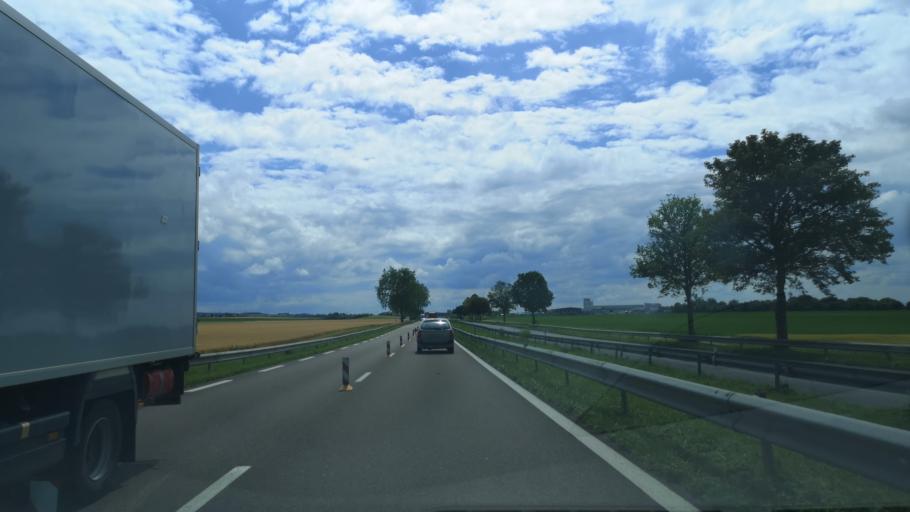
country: FR
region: Champagne-Ardenne
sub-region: Departement de la Marne
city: Bazancourt
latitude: 49.3219
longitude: 4.1596
